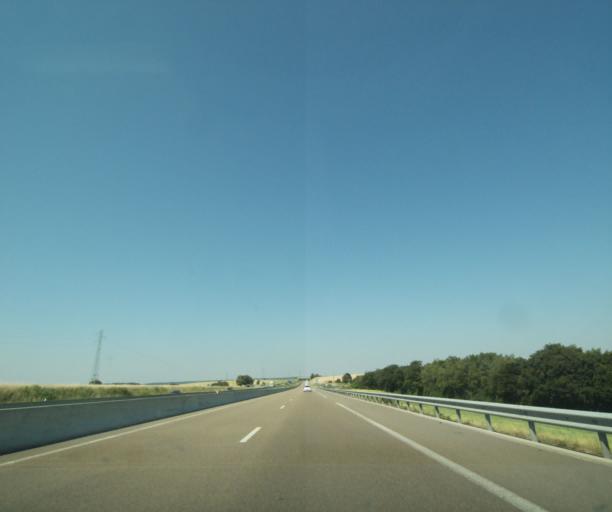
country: FR
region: Lorraine
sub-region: Departement de la Meuse
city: Ligny-en-Barrois
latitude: 48.6970
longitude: 5.3777
